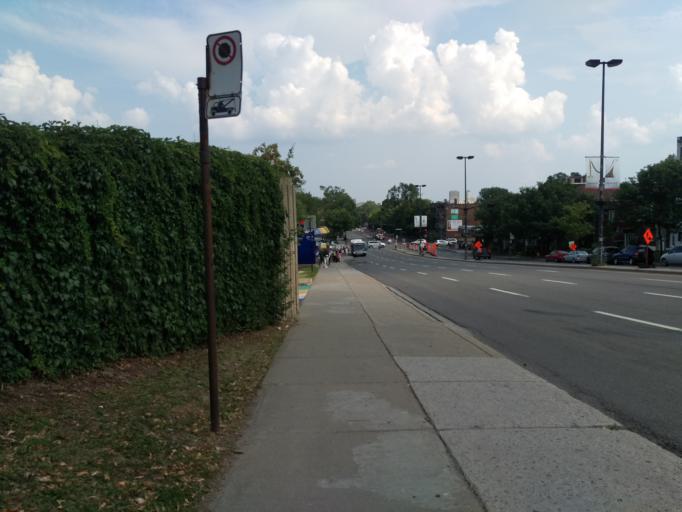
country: CA
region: Quebec
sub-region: Monteregie
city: Longueuil
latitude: 45.5544
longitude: -73.5535
